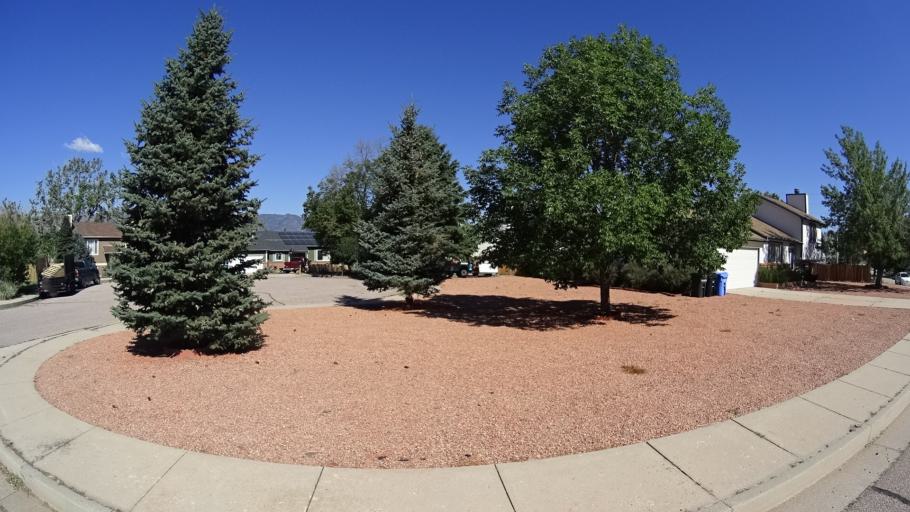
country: US
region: Colorado
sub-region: El Paso County
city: Air Force Academy
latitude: 38.9427
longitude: -104.7852
